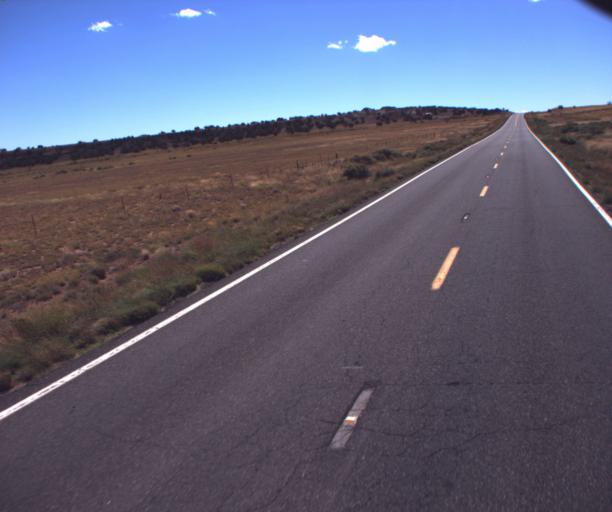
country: US
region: Arizona
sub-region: Apache County
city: Saint Johns
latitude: 34.7617
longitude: -109.2423
